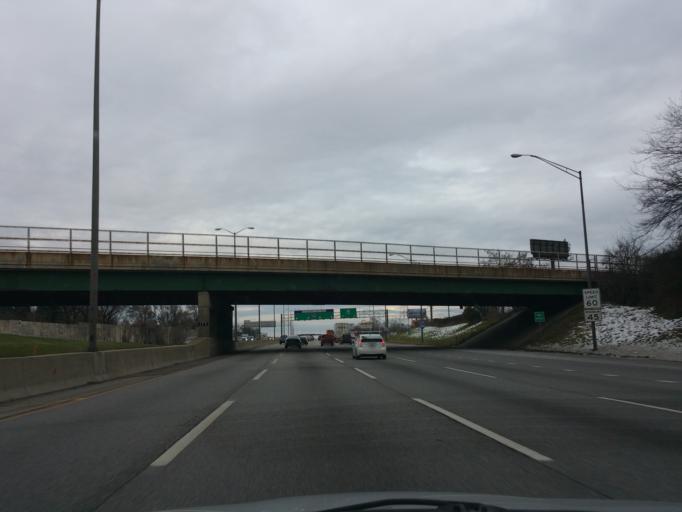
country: US
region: Illinois
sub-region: Cook County
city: Justice
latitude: 41.7452
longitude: -87.8388
